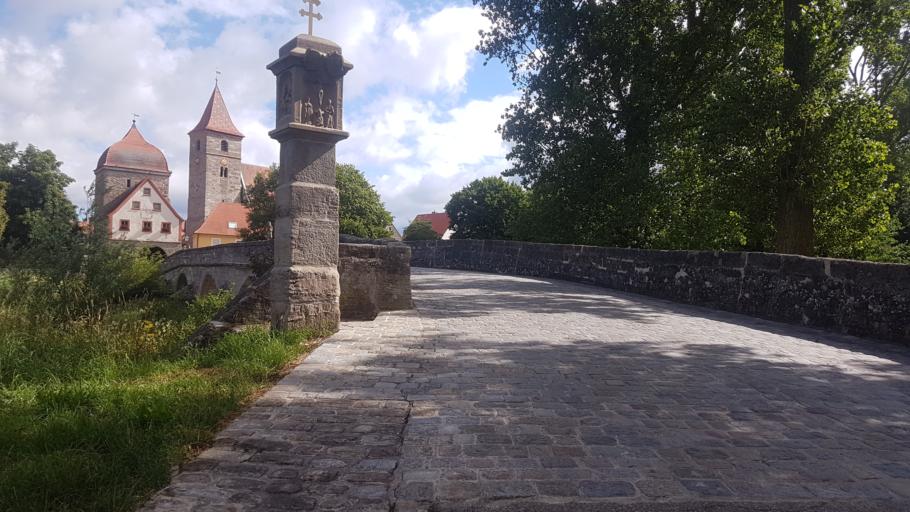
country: DE
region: Bavaria
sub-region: Regierungsbezirk Mittelfranken
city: Ornbau
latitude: 49.1737
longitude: 10.6555
